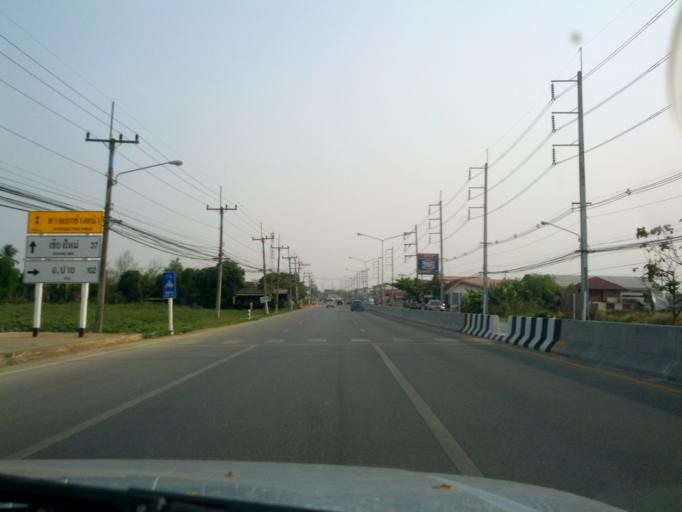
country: TH
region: Chiang Mai
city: Mae Taeng
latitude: 19.1034
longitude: 98.9362
